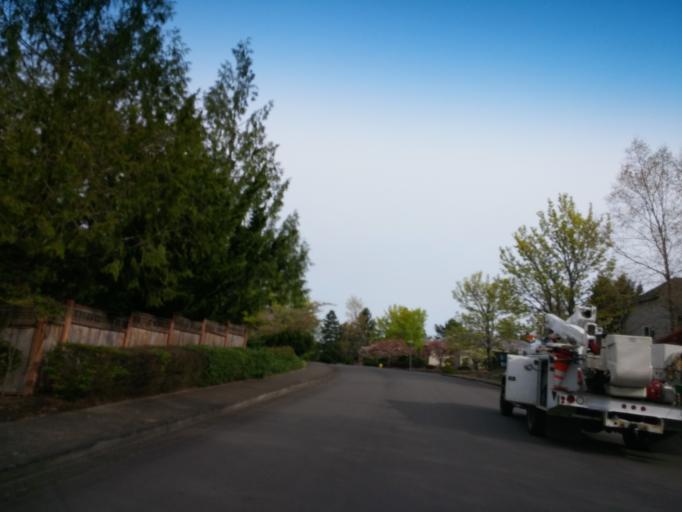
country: US
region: Oregon
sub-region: Washington County
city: Cedar Mill
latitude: 45.5395
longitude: -122.8129
